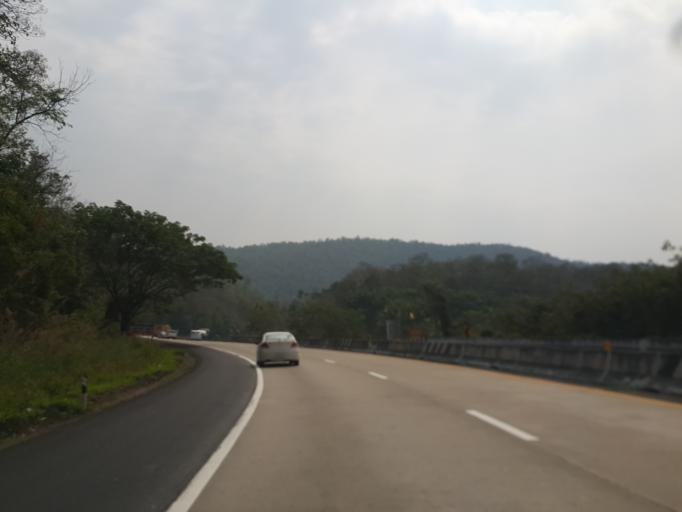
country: TH
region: Lampang
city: Hang Chat
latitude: 18.3324
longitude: 99.2515
